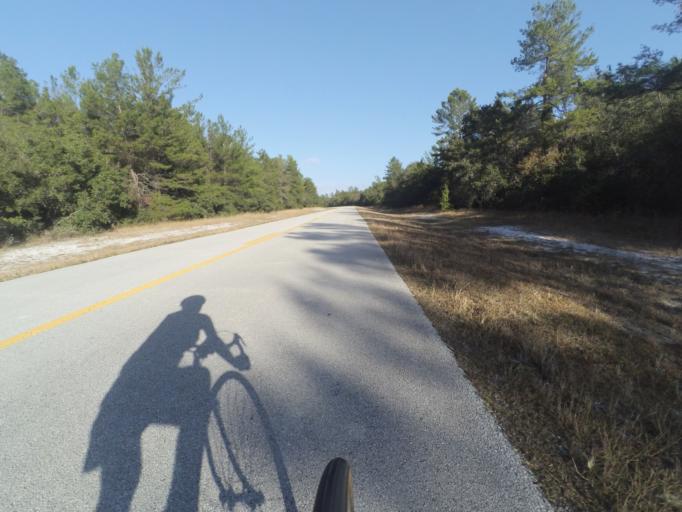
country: US
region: Florida
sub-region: Lake County
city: Astor
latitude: 29.0993
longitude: -81.5651
